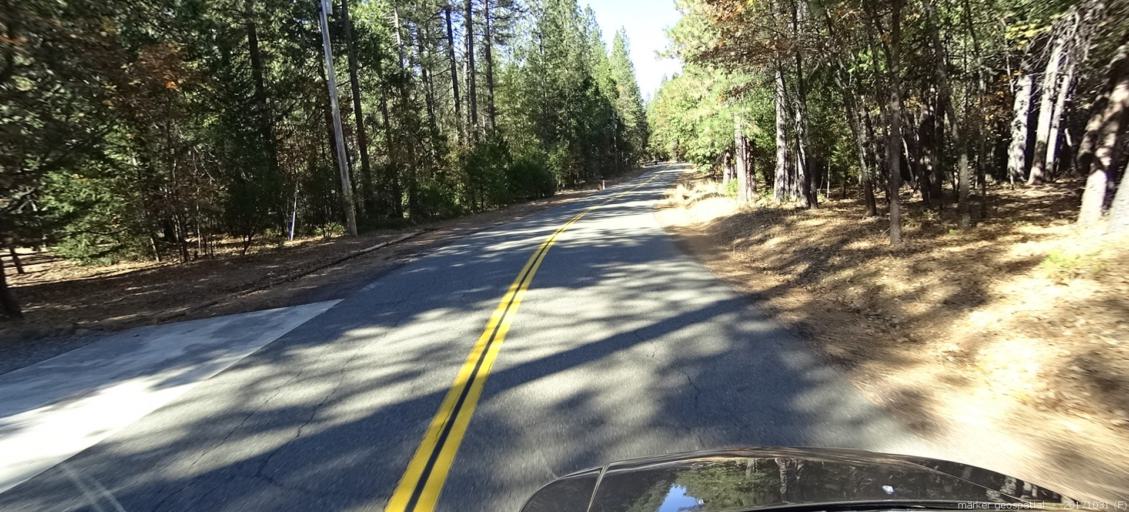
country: US
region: California
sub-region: Shasta County
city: Shingletown
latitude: 40.4857
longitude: -121.8814
